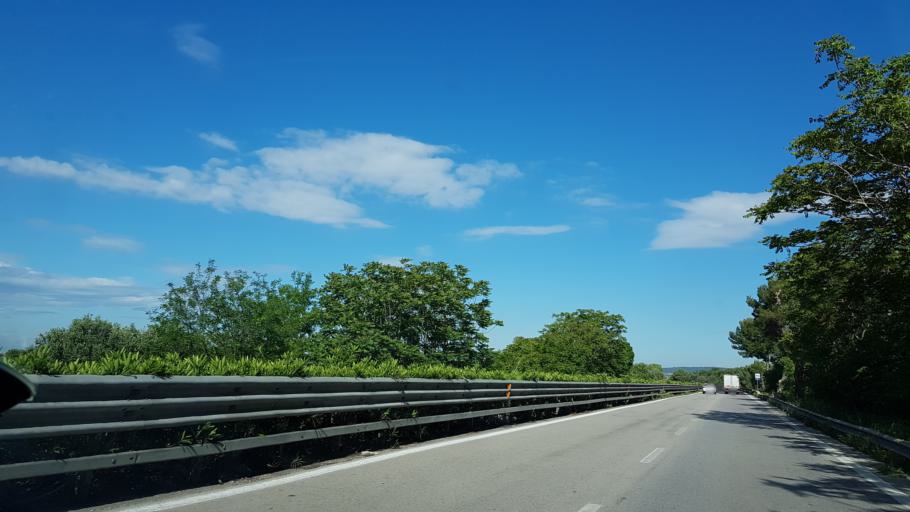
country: IT
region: Apulia
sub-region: Provincia di Taranto
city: Grottaglie
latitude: 40.5294
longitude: 17.4097
